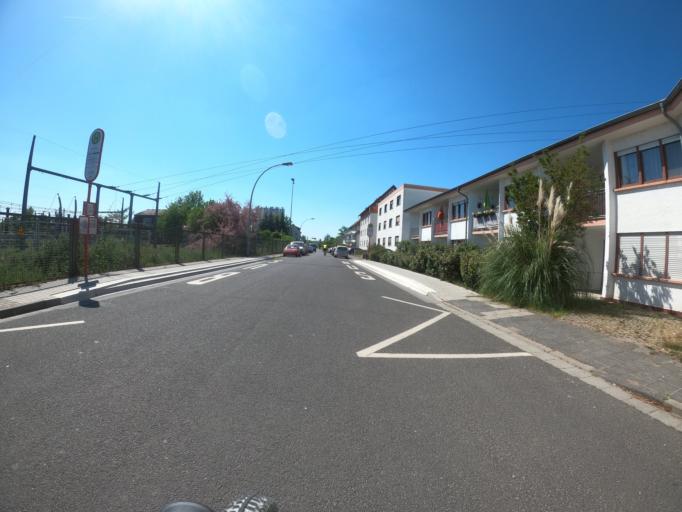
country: DE
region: Hesse
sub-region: Regierungsbezirk Darmstadt
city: Florsheim
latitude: 50.0054
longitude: 8.4152
